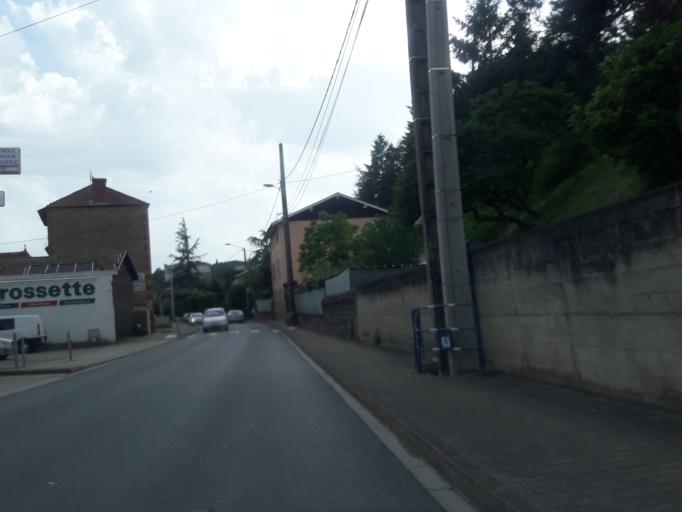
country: FR
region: Rhone-Alpes
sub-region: Departement du Rhone
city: Sain-Bel
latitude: 45.8297
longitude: 4.6101
